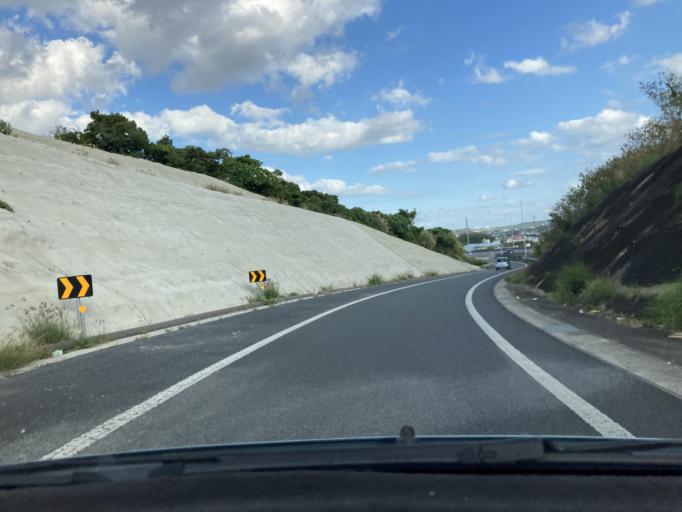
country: JP
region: Okinawa
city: Tomigusuku
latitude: 26.1730
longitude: 127.6970
